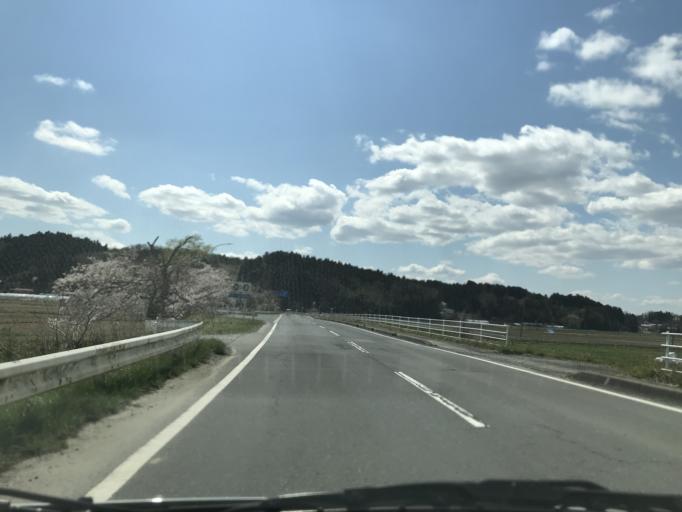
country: JP
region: Miyagi
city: Wakuya
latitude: 38.6481
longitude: 141.2576
